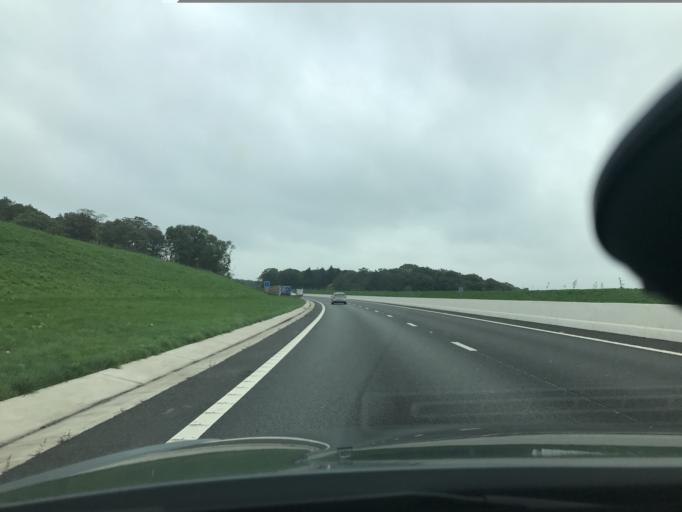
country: GB
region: England
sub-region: Cheshire East
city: Mere
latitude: 53.3305
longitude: -2.4223
